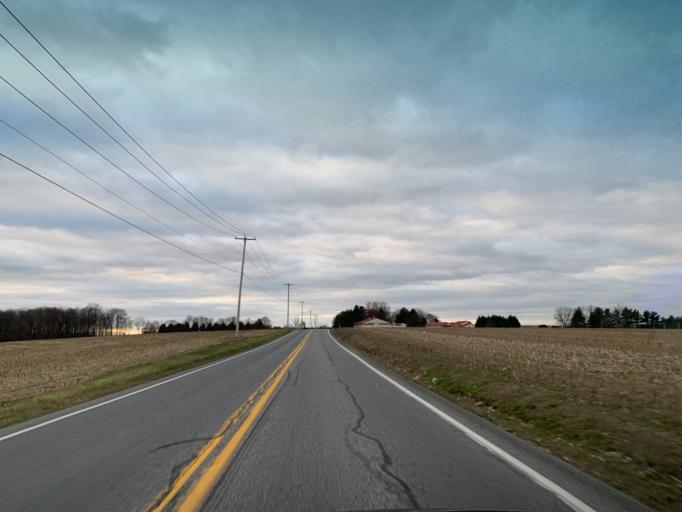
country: US
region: Pennsylvania
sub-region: York County
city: Shrewsbury
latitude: 39.7852
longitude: -76.6518
